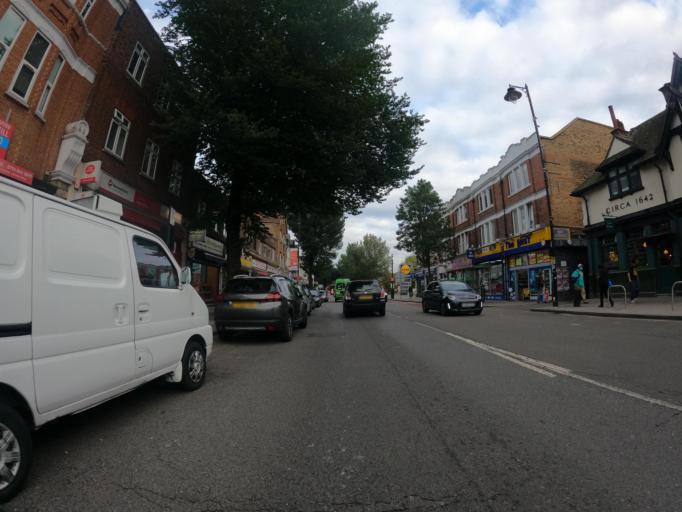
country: GB
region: England
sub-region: Greater London
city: Greenford
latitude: 51.5088
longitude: -0.3372
